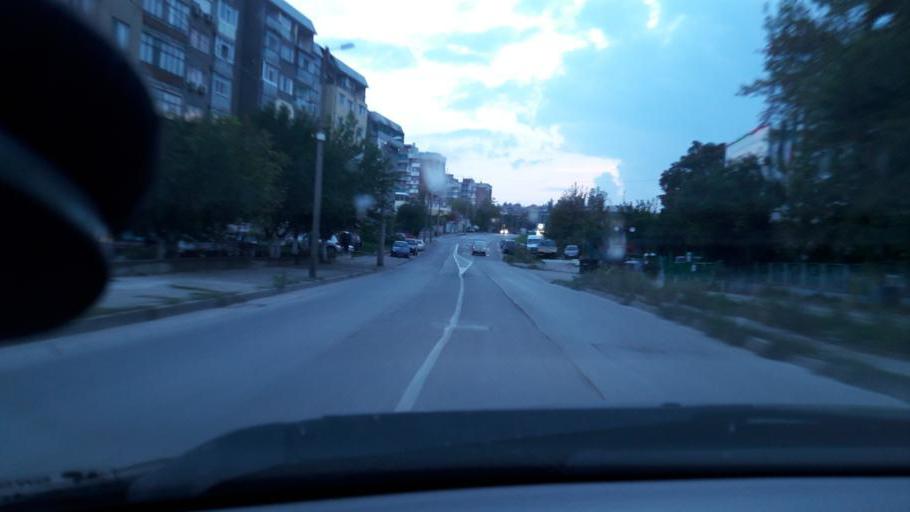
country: BG
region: Razgrad
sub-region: Obshtina Razgrad
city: Razgrad
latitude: 43.5317
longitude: 26.5146
